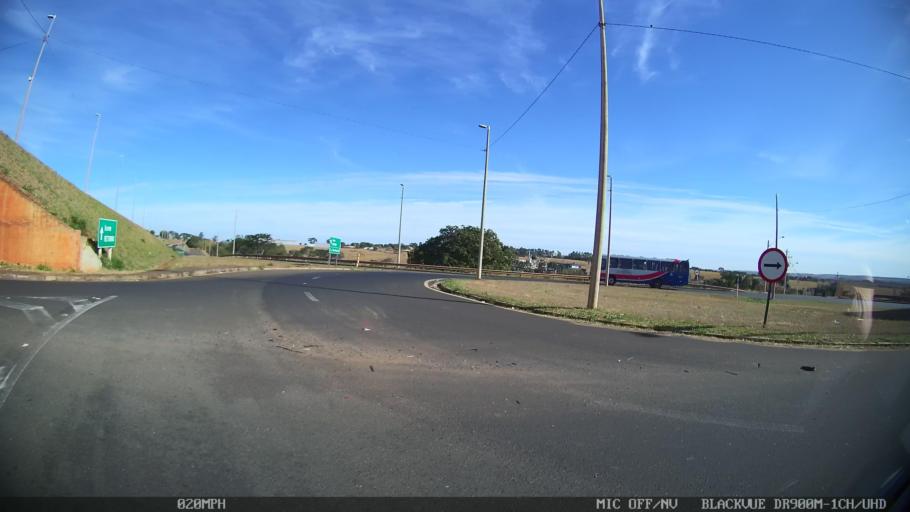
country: BR
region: Sao Paulo
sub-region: Sao Jose Do Rio Preto
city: Sao Jose do Rio Preto
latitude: -20.7350
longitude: -49.3386
